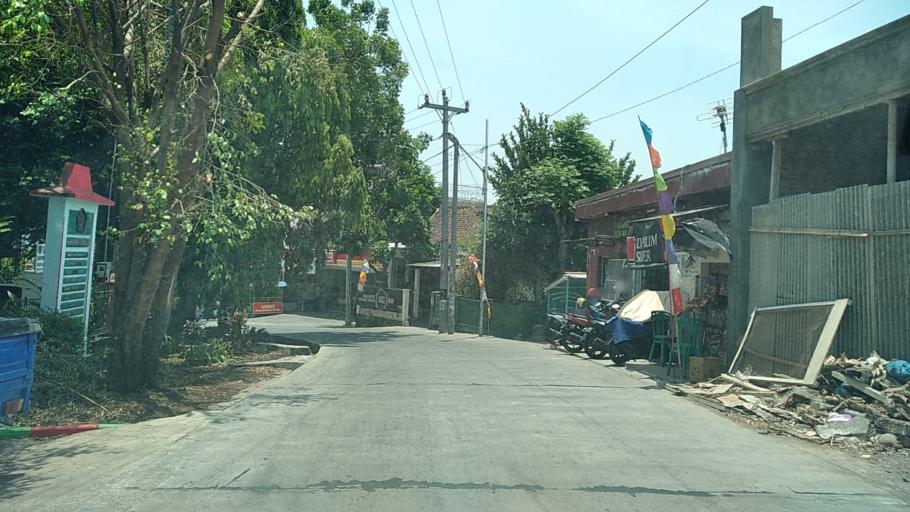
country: ID
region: Central Java
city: Semarang
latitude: -7.0132
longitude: 110.4541
